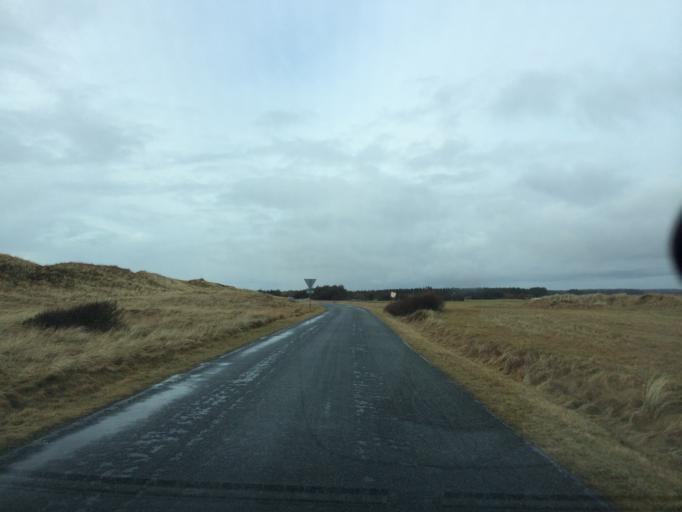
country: DK
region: Central Jutland
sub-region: Holstebro Kommune
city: Ulfborg
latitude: 56.2444
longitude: 8.1388
